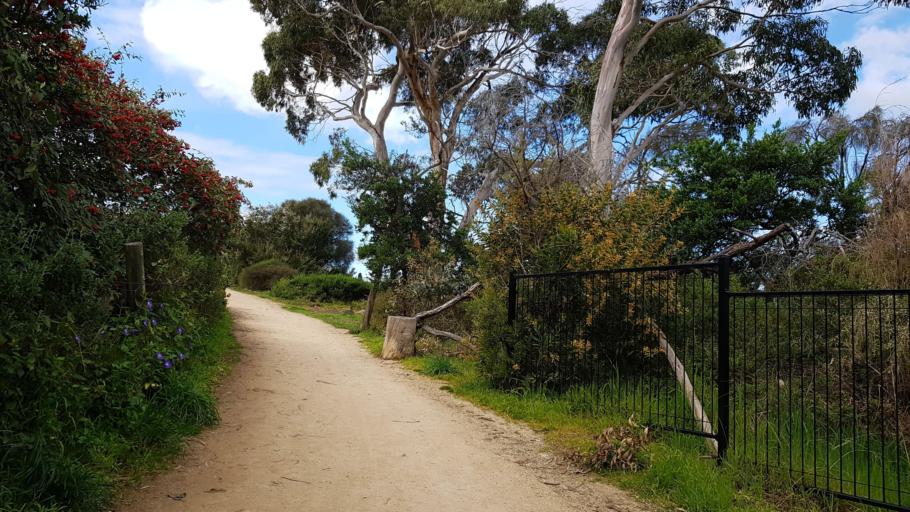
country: AU
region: Tasmania
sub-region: Clarence
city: Bellerive
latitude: -42.8817
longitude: 147.3858
